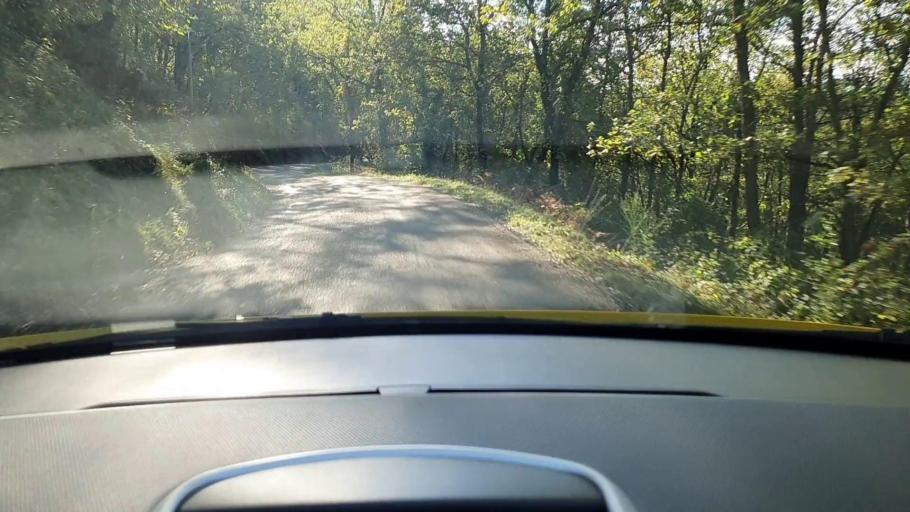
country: FR
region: Languedoc-Roussillon
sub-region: Departement du Gard
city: Sumene
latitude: 44.0002
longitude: 3.7740
